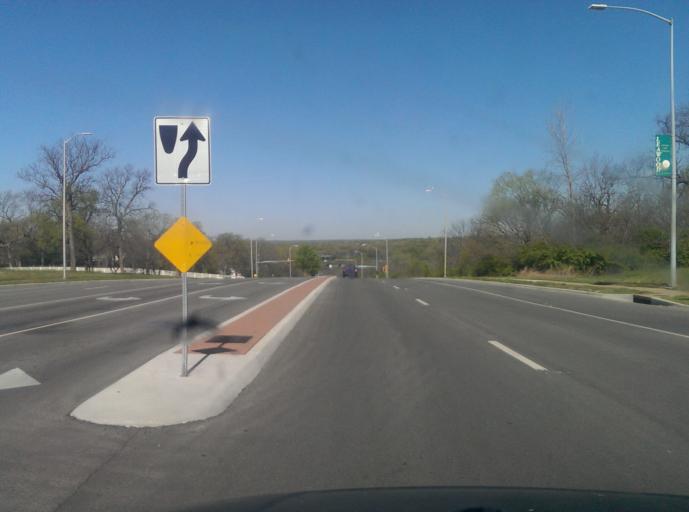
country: US
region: Kansas
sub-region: Johnson County
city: Leawood
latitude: 38.9294
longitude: -94.6083
